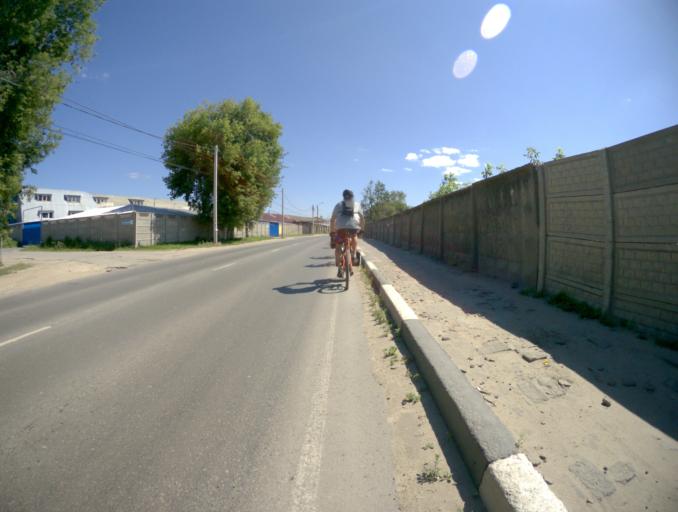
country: RU
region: Nizjnij Novgorod
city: Bor
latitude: 56.3608
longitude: 44.0671
